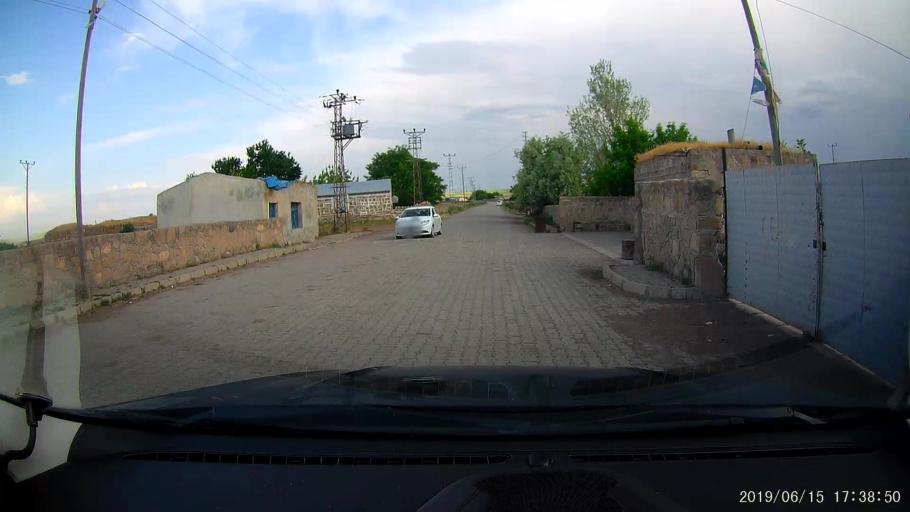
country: TR
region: Kars
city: Basgedikler
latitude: 40.5190
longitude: 43.5683
